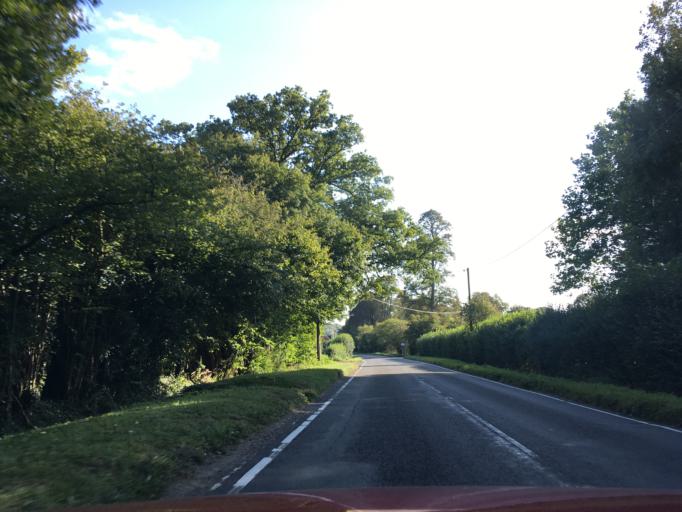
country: GB
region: England
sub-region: Hampshire
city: Alton
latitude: 51.1058
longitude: -0.9937
